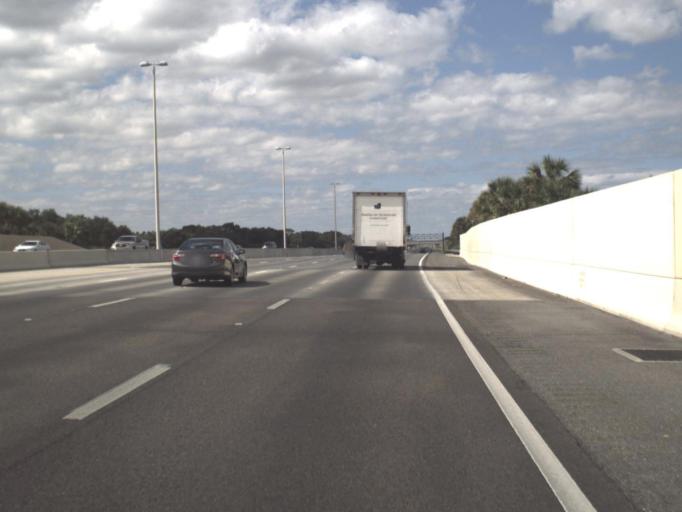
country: US
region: Florida
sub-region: Orange County
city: Winter Garden
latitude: 28.5455
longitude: -81.5696
